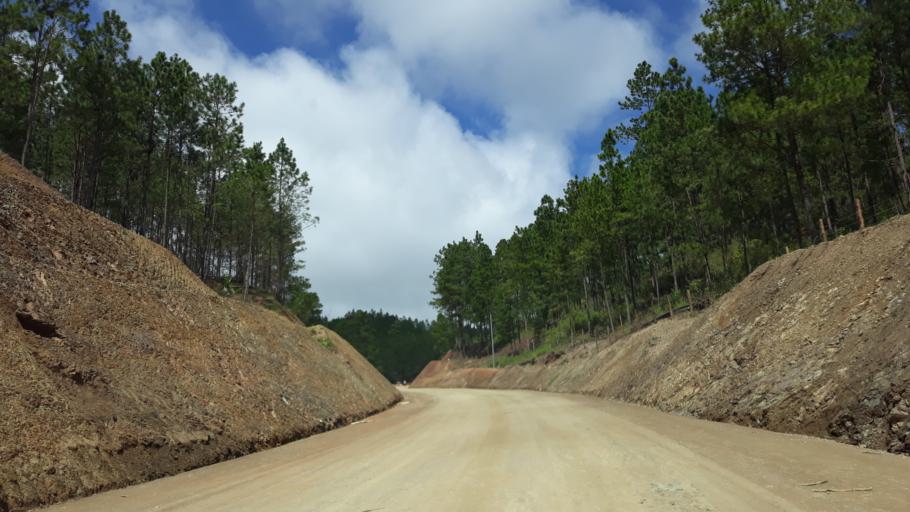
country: HN
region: El Paraiso
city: Santa Cruz
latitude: 13.7677
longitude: -86.6396
